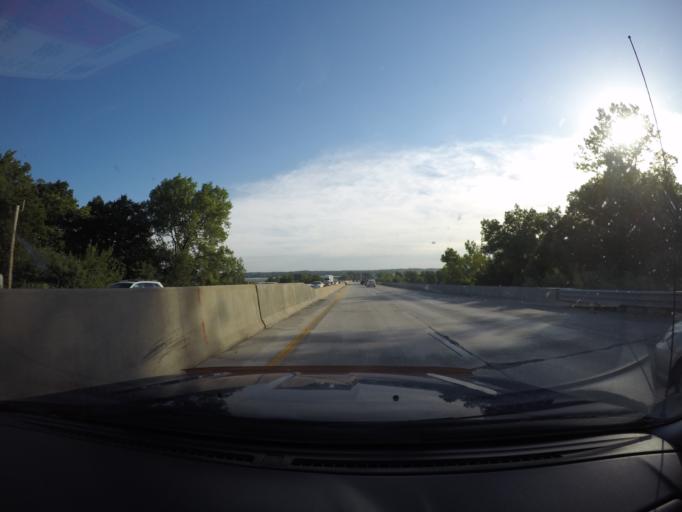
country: US
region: Kansas
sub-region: Wyandotte County
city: Kansas City
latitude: 39.1523
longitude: -94.6519
